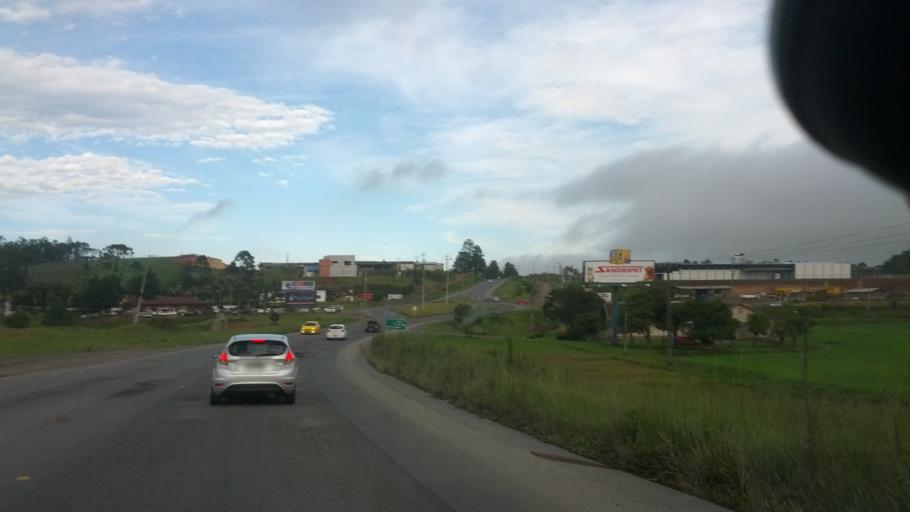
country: BR
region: Santa Catarina
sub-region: Otacilio Costa
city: Otacilio Costa
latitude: -27.2519
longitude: -49.9576
